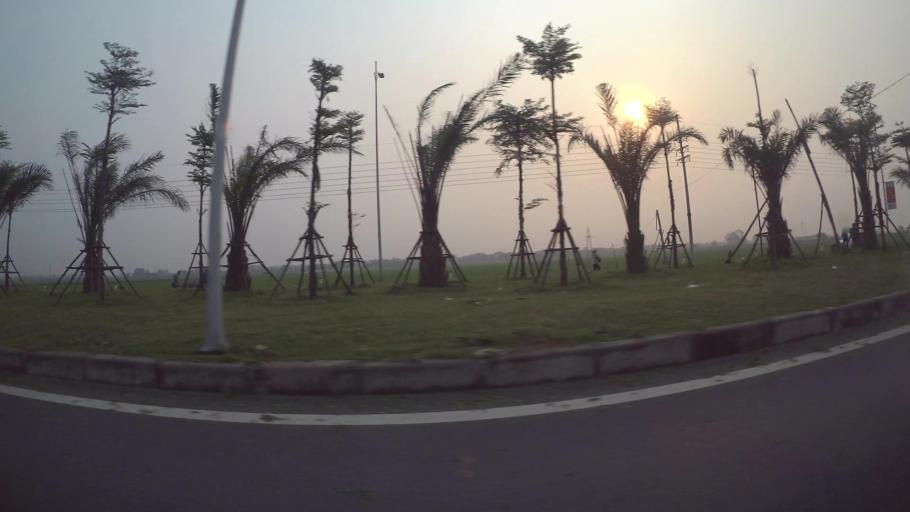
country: VN
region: Ha Noi
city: Kim Bai
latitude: 20.8878
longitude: 105.7963
